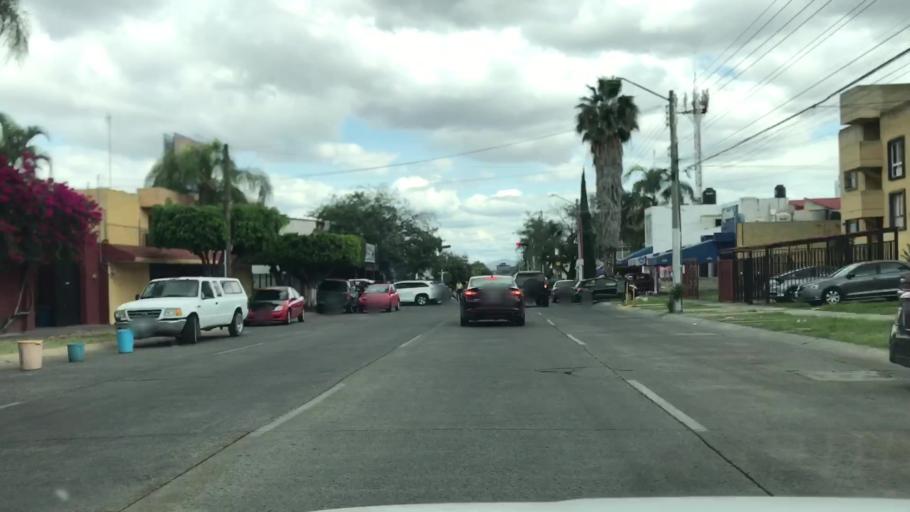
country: MX
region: Jalisco
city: Guadalajara
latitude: 20.6361
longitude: -103.4285
